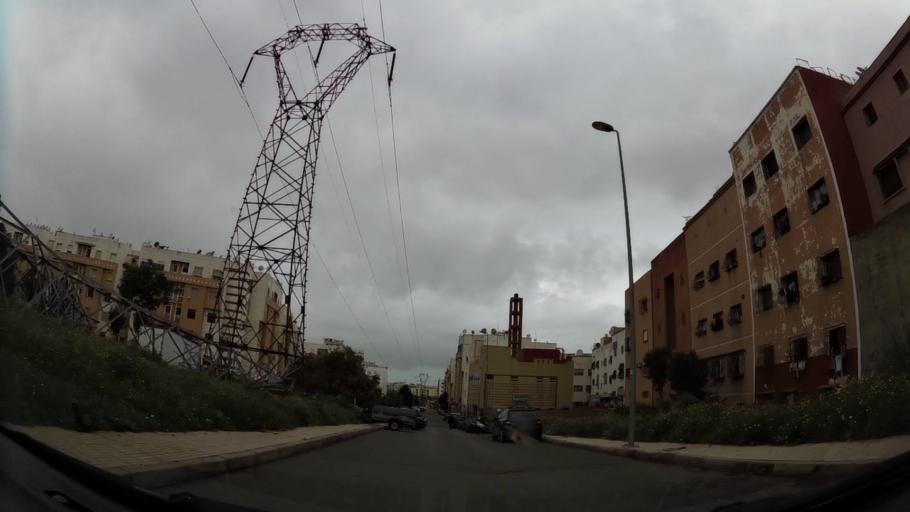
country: MA
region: Grand Casablanca
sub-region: Casablanca
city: Casablanca
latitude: 33.5316
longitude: -7.6106
